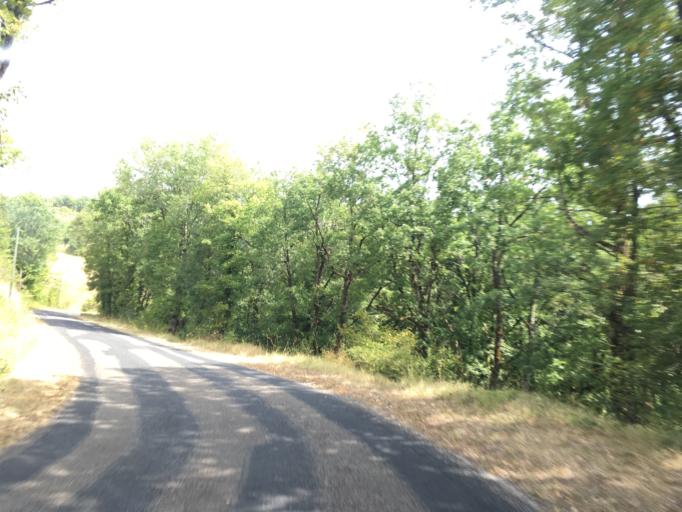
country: FR
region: Midi-Pyrenees
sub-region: Departement du Lot
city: Le Vigan
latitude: 44.7478
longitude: 1.5025
